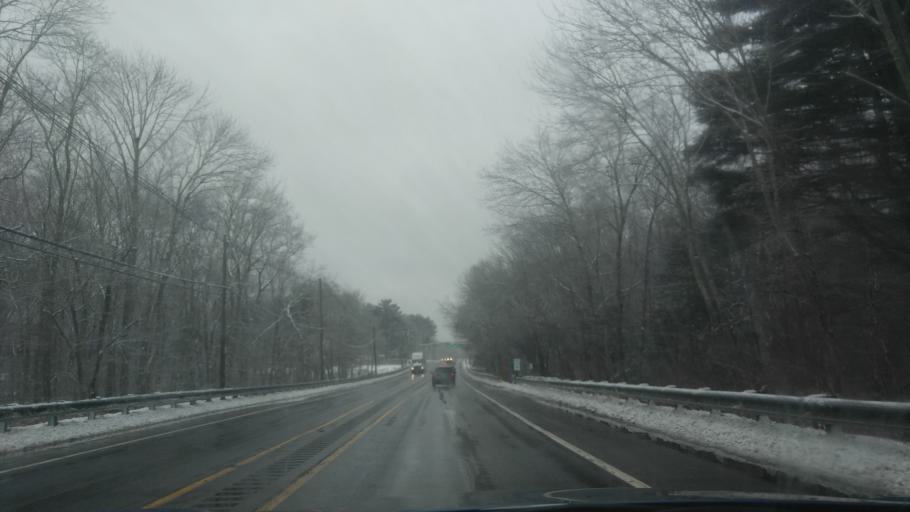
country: US
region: Rhode Island
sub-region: Providence County
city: Foster
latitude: 41.8154
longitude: -71.7308
